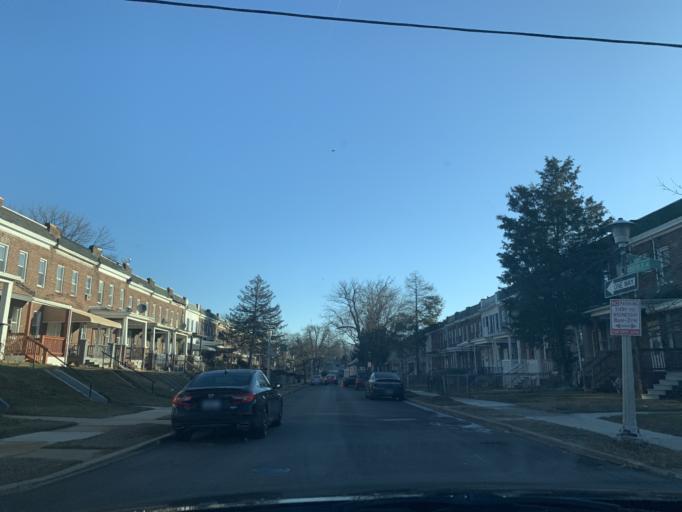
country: US
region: Maryland
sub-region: Baltimore County
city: Lochearn
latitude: 39.3232
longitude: -76.6881
